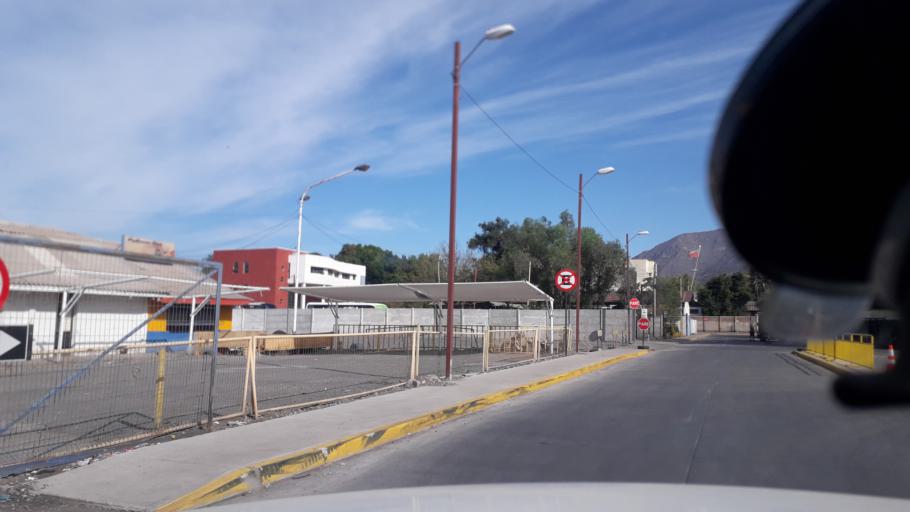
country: CL
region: Valparaiso
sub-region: Provincia de San Felipe
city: San Felipe
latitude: -32.7538
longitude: -70.7193
